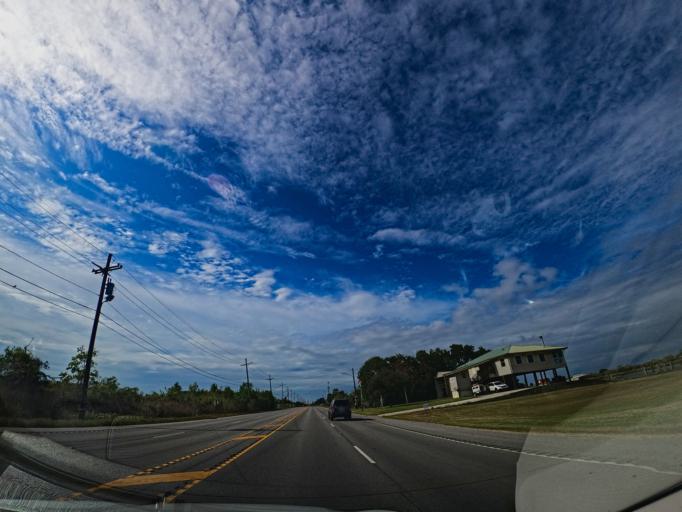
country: US
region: Louisiana
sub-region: Saint Tammany Parish
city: Eden Isle
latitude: 30.0706
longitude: -89.8379
